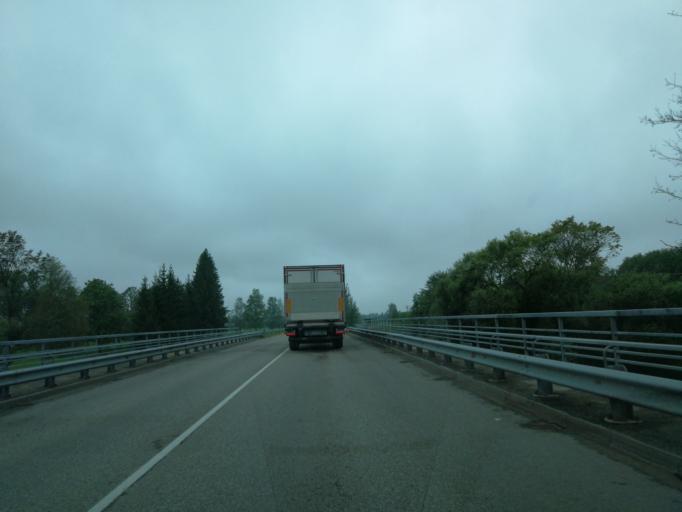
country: LV
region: Livani
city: Livani
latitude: 56.3414
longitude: 26.3469
